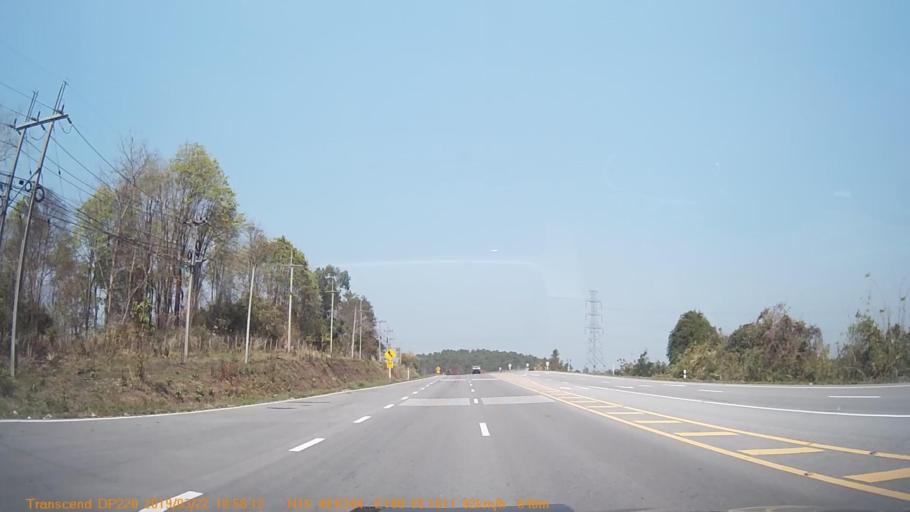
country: TH
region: Phetchabun
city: Khao Kho
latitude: 16.8275
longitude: 100.9191
